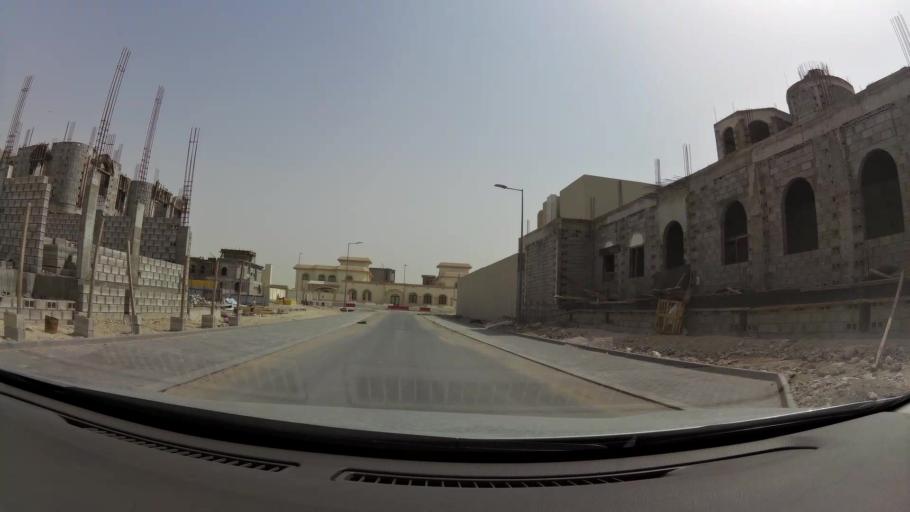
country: QA
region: Baladiyat ar Rayyan
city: Ar Rayyan
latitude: 25.2600
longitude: 51.3691
